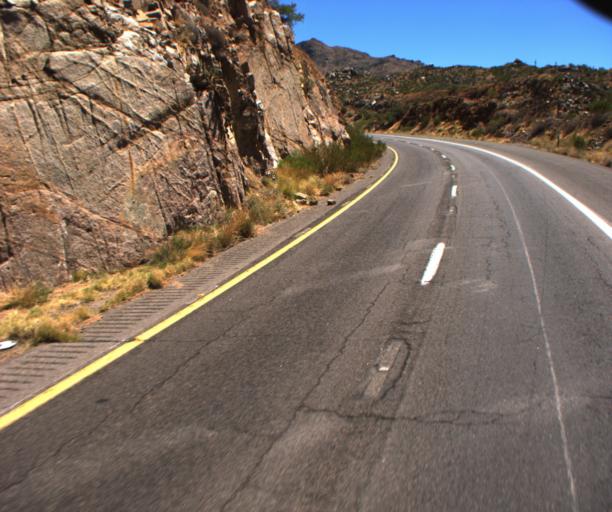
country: US
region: Arizona
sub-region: Gila County
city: Tonto Basin
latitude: 33.8167
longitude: -111.4804
